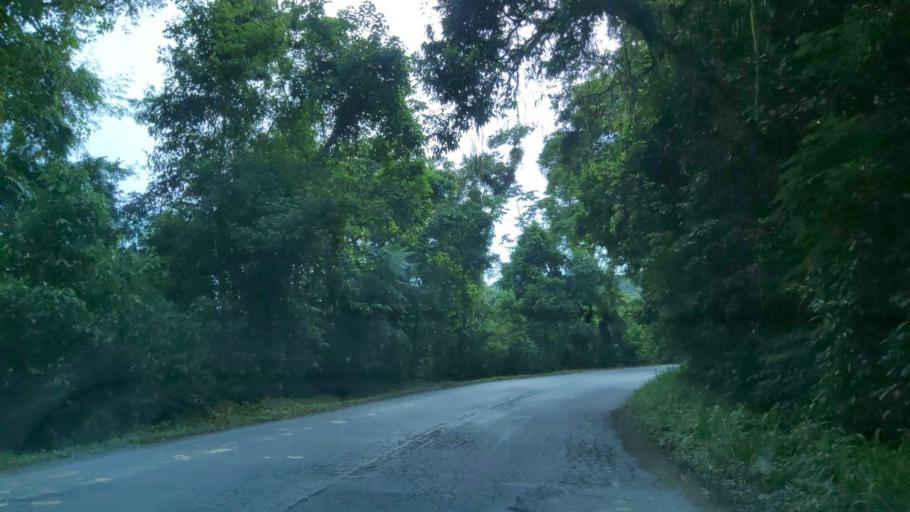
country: BR
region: Sao Paulo
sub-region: Juquia
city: Juquia
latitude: -24.0681
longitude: -47.6017
